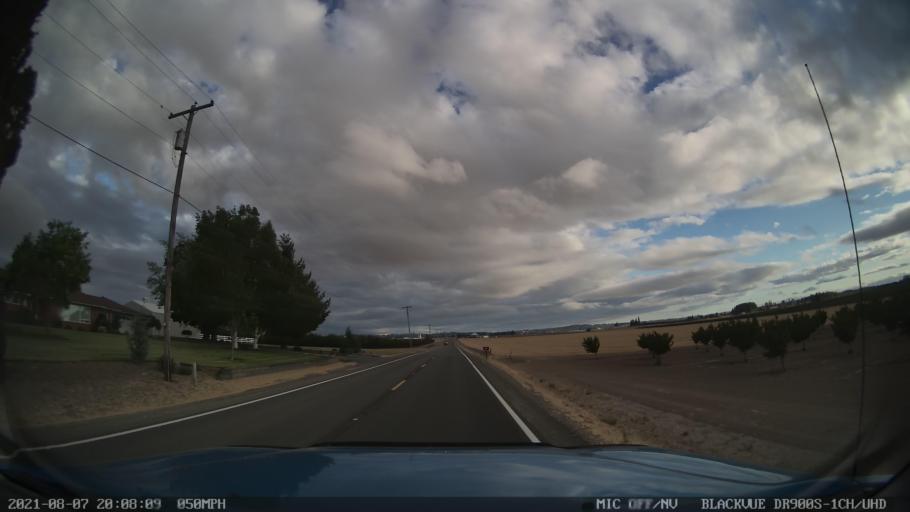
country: US
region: Oregon
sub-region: Marion County
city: Silverton
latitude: 44.9844
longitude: -122.8805
